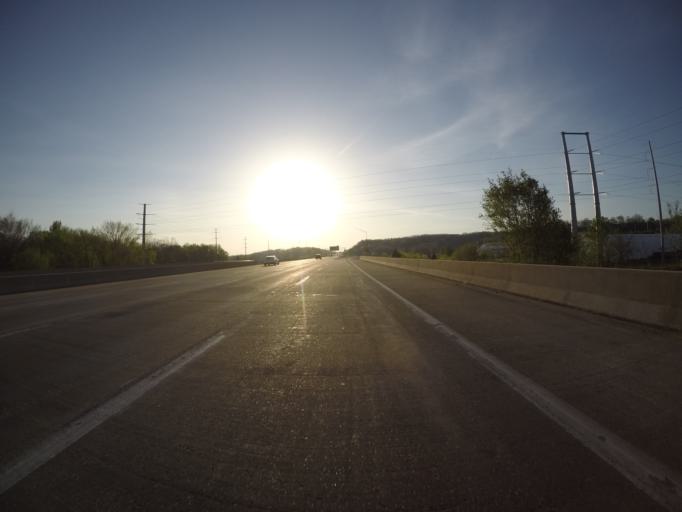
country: US
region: Missouri
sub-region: Jackson County
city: Raytown
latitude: 38.9365
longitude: -94.4523
